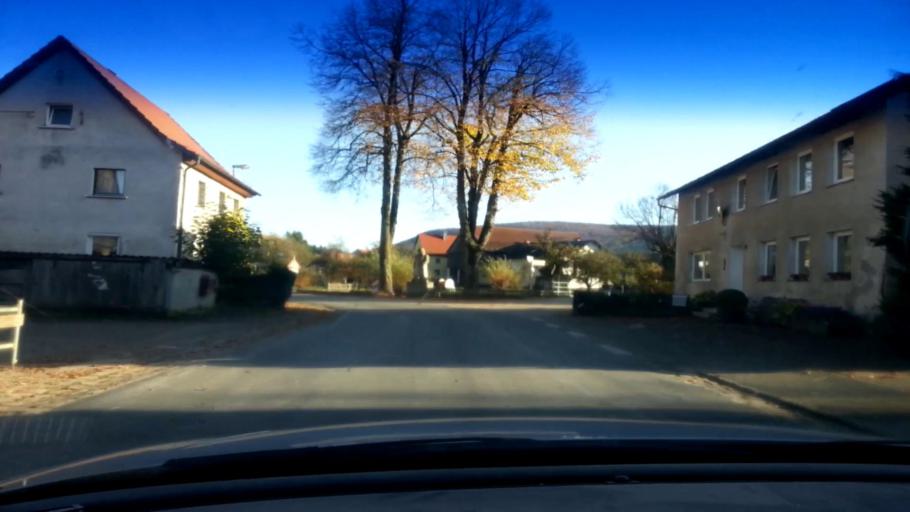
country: DE
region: Bavaria
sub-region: Upper Franconia
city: Heiligenstadt
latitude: 49.8824
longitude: 11.1296
